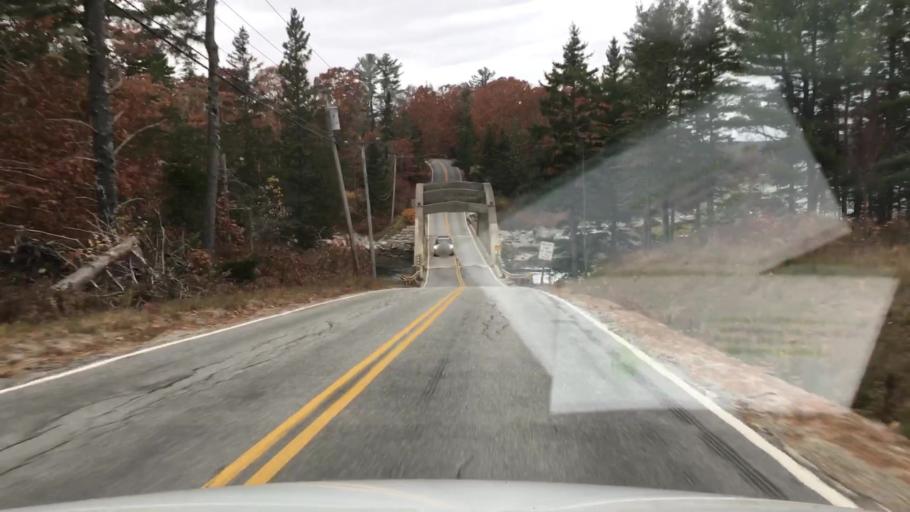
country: US
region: Maine
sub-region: Hancock County
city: Sedgwick
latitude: 44.3732
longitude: -68.5589
